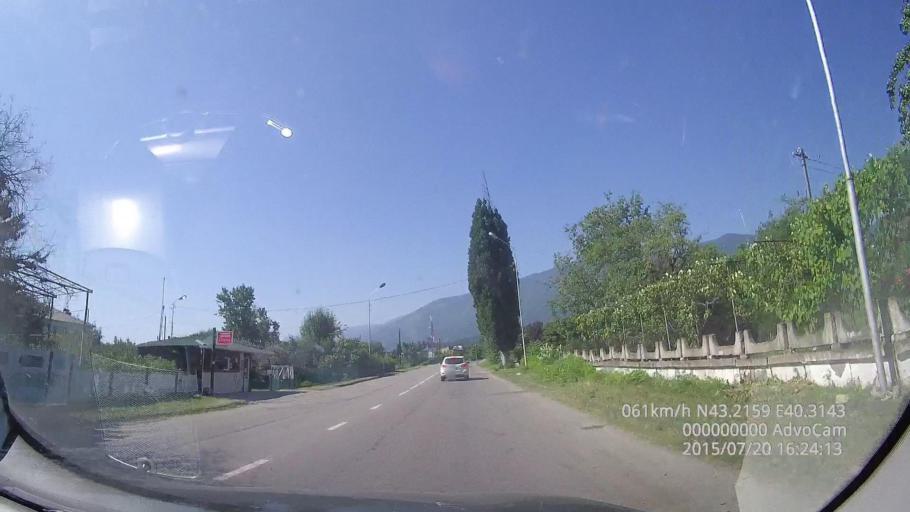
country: GE
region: Abkhazia
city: Bich'vinta
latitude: 43.2159
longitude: 40.3143
